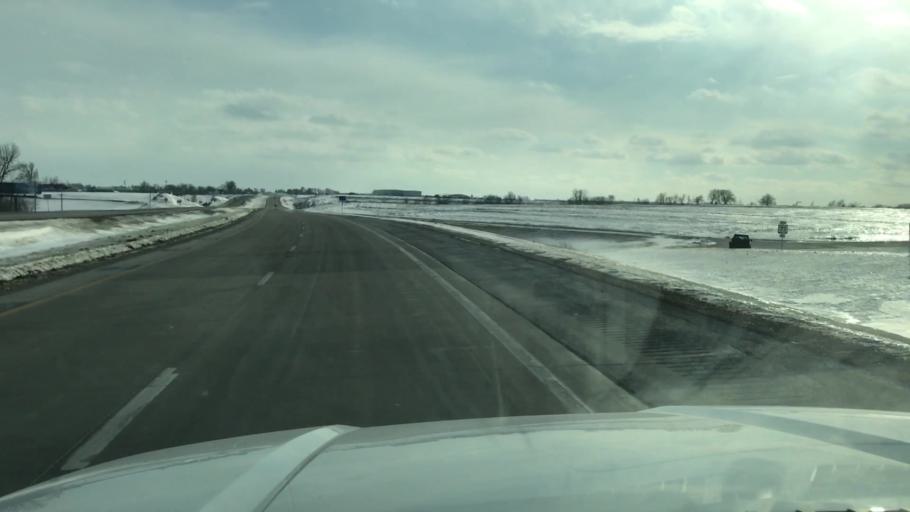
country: US
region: Missouri
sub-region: Nodaway County
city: Maryville
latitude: 40.3105
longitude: -94.8746
